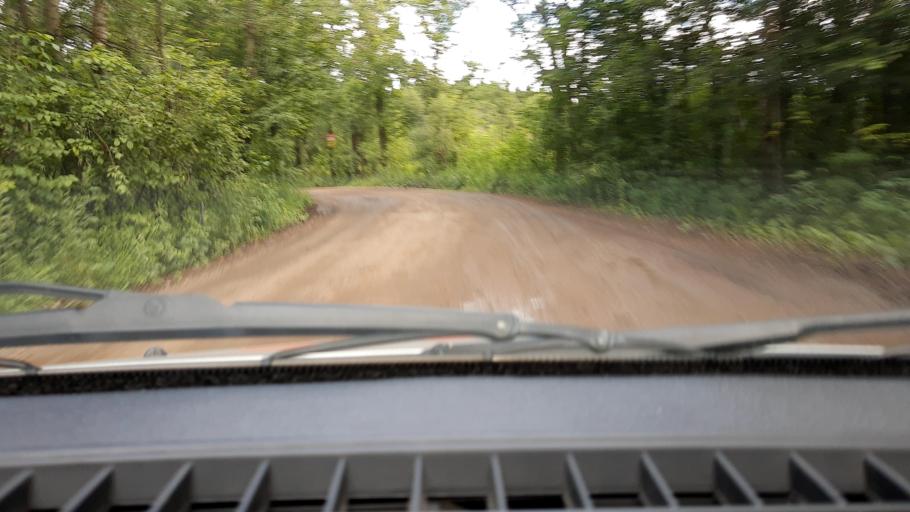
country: RU
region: Bashkortostan
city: Ufa
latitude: 54.6817
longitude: 56.0606
